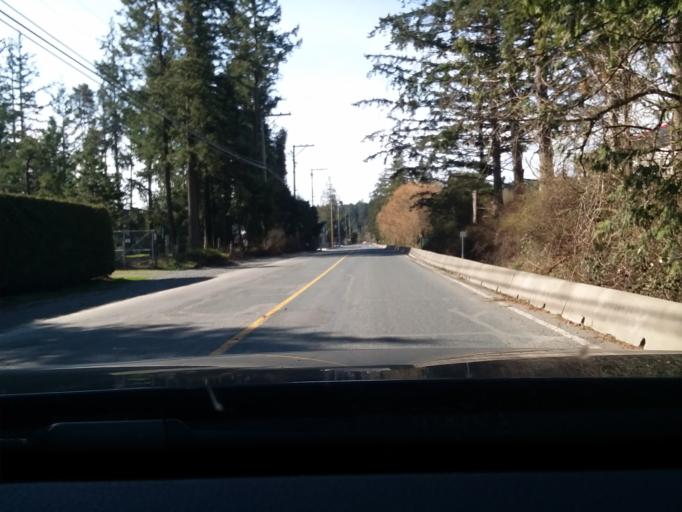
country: CA
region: British Columbia
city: Langford
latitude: 48.4268
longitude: -123.5364
